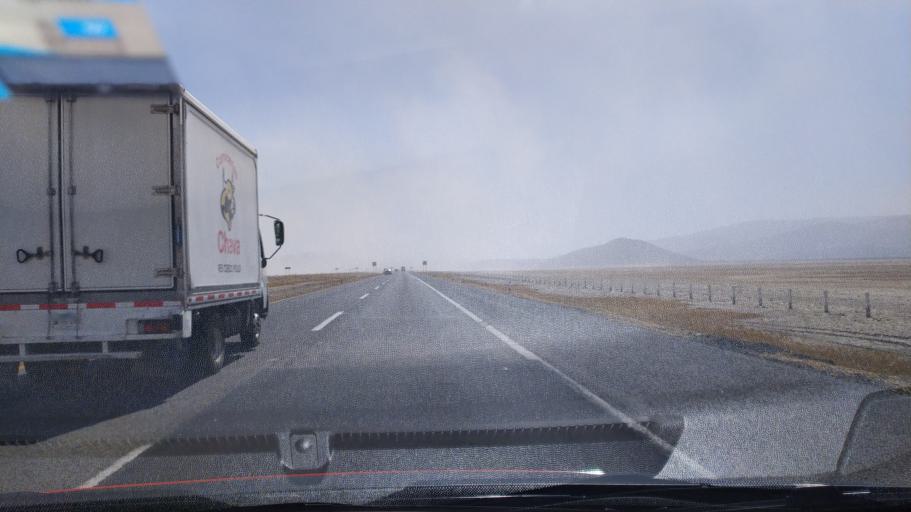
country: MX
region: Jalisco
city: Zacoalco de Torres
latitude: 20.3138
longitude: -103.5632
